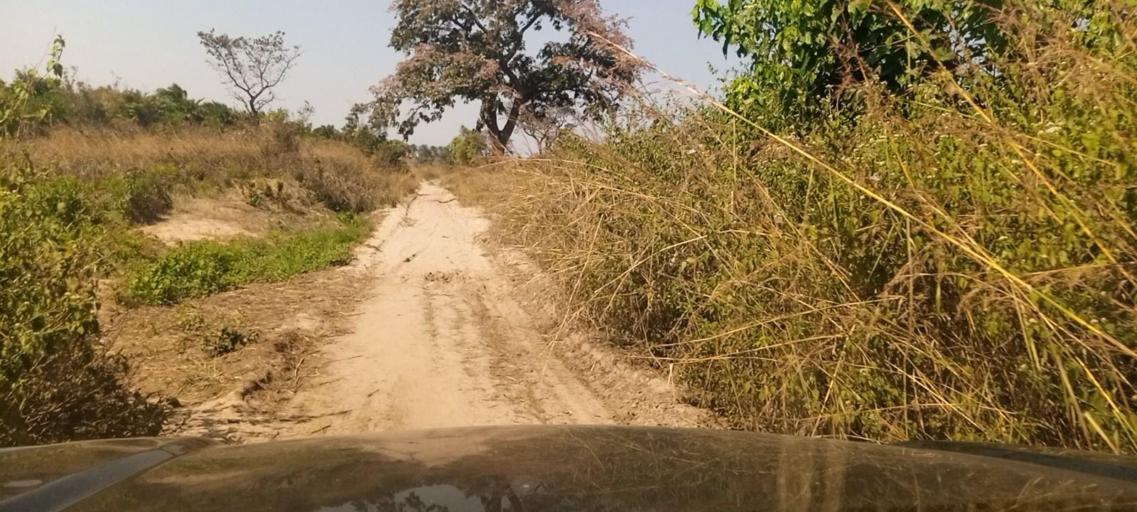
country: CD
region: Kasai-Oriental
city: Kabinda
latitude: -5.7802
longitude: 25.0602
